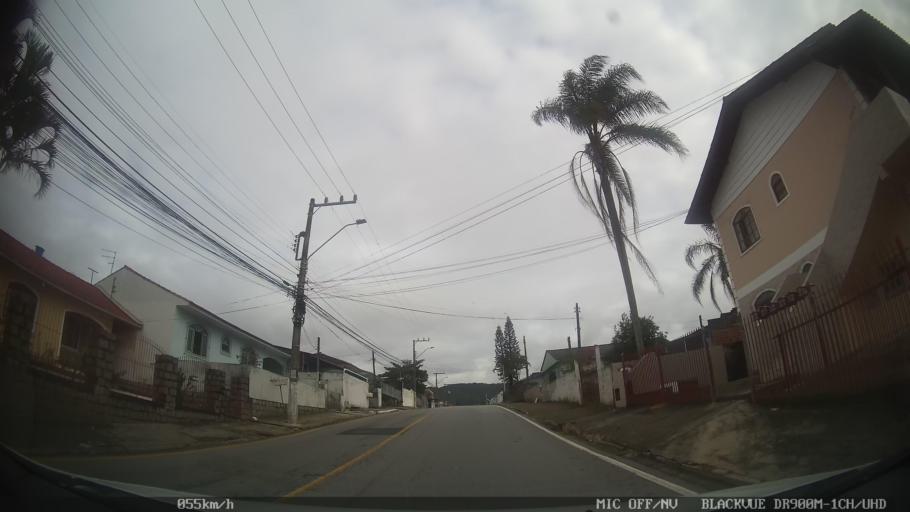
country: BR
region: Santa Catarina
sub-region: Biguacu
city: Biguacu
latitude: -27.5424
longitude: -48.6367
